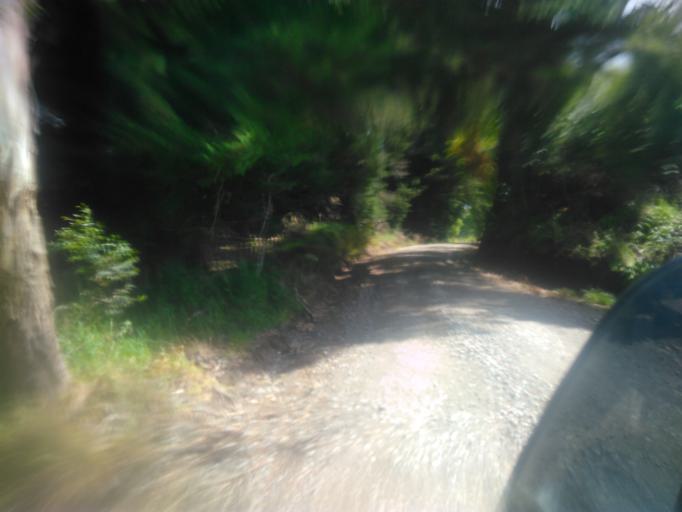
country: NZ
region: Hawke's Bay
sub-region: Wairoa District
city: Wairoa
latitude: -38.7614
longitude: 177.5946
